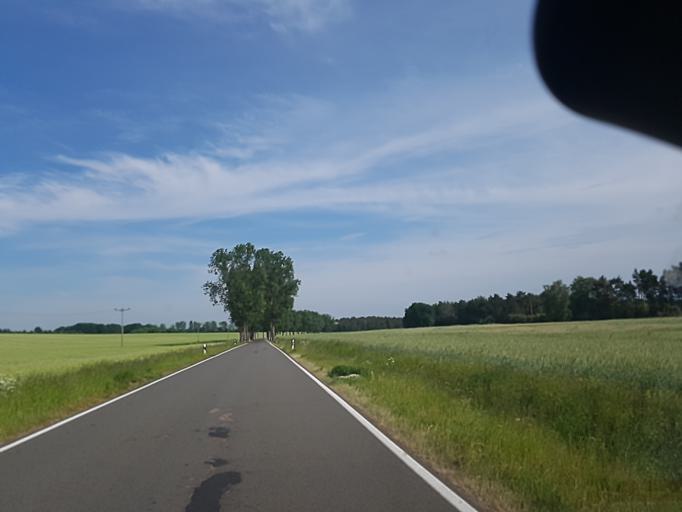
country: DE
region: Saxony-Anhalt
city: Kropstadt
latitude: 51.9742
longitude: 12.7291
